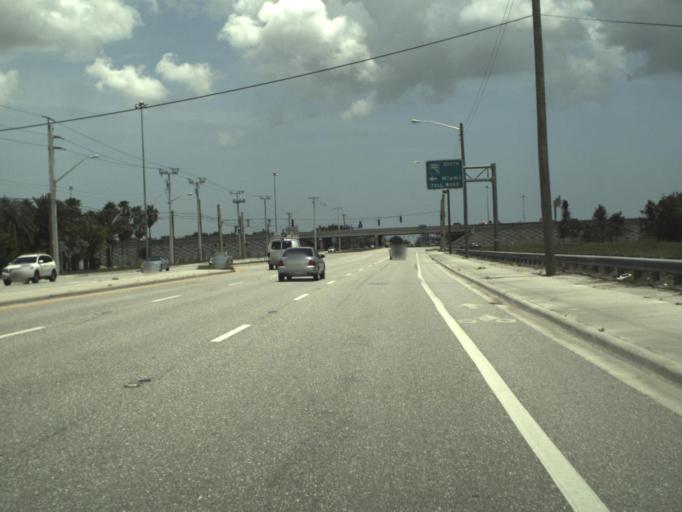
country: US
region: Florida
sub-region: Palm Beach County
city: Villages of Oriole
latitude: 26.5279
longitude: -80.1766
